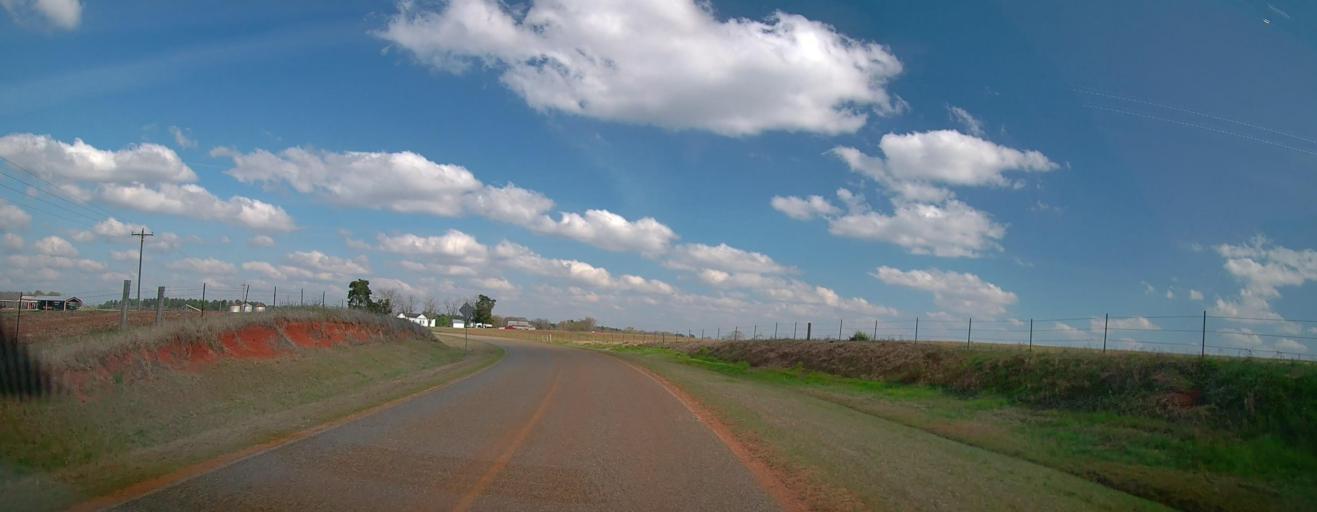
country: US
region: Georgia
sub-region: Twiggs County
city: Jeffersonville
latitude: 32.6539
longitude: -83.2145
